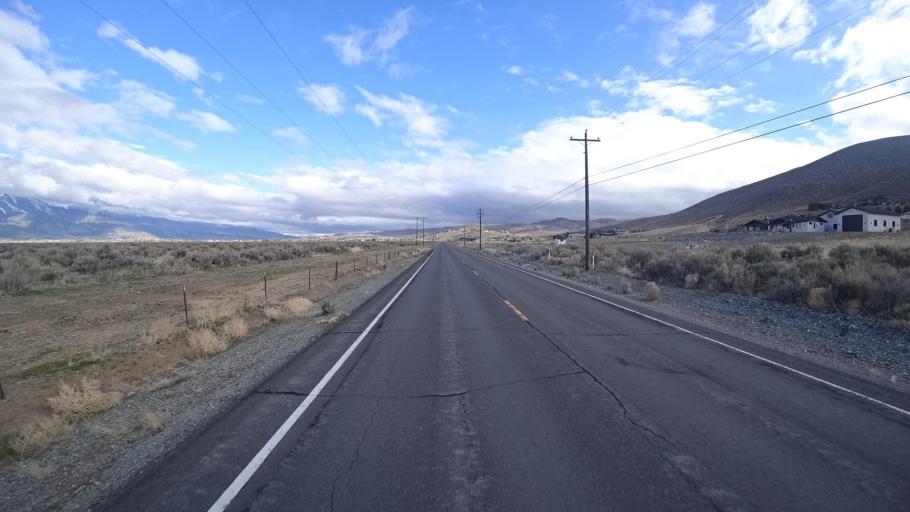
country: US
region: Nevada
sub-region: Carson City
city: Carson City
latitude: 39.2623
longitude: -119.7566
